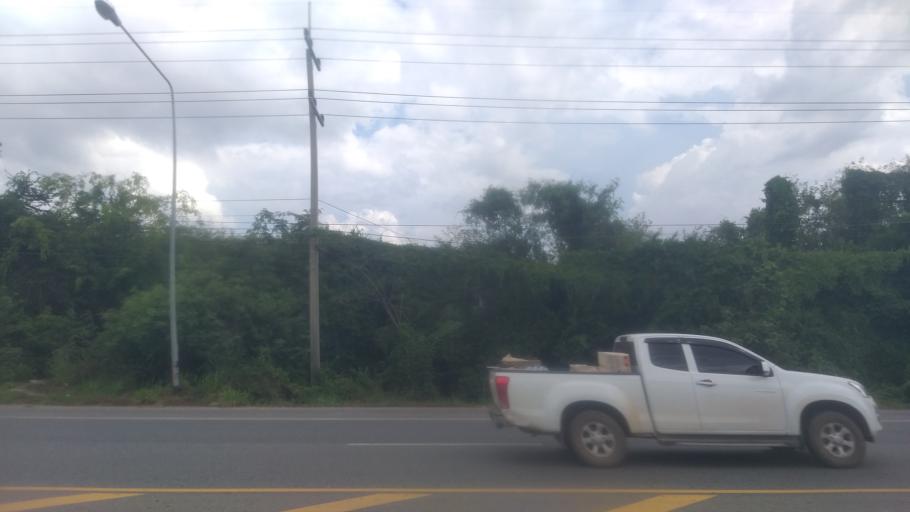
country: TH
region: Chaiyaphum
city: Noen Sa-nga
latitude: 15.6765
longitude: 101.9840
